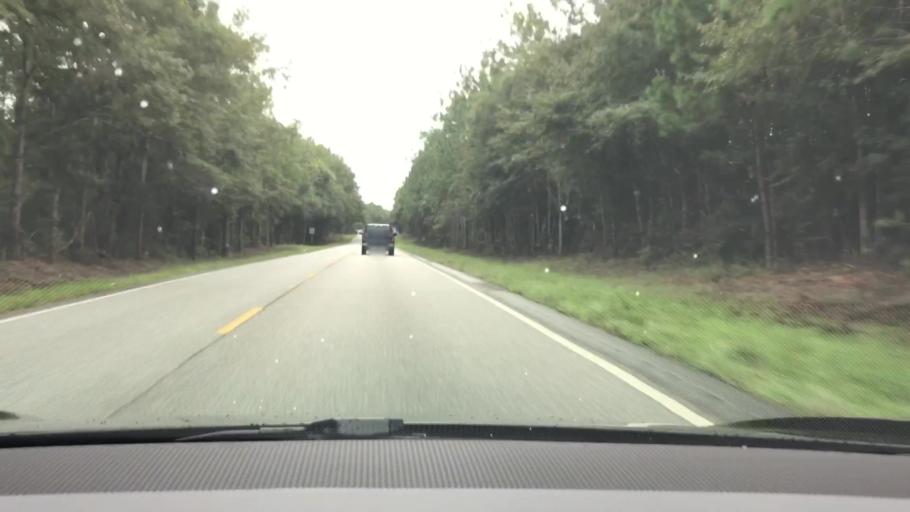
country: US
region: Alabama
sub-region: Geneva County
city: Samson
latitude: 30.9969
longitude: -86.1325
